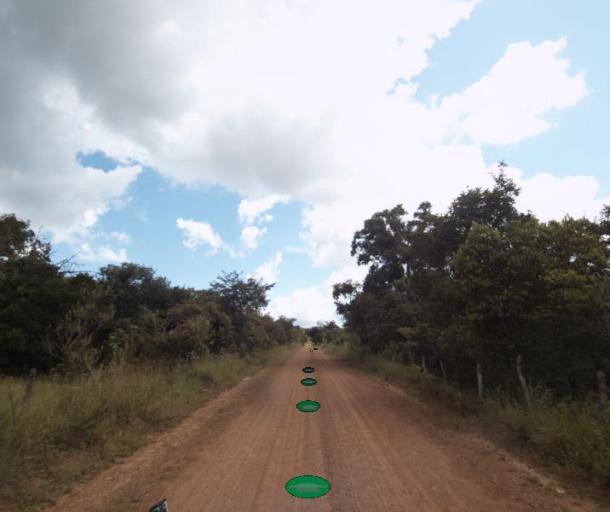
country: BR
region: Goias
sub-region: Pirenopolis
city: Pirenopolis
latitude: -15.7907
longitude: -48.8845
